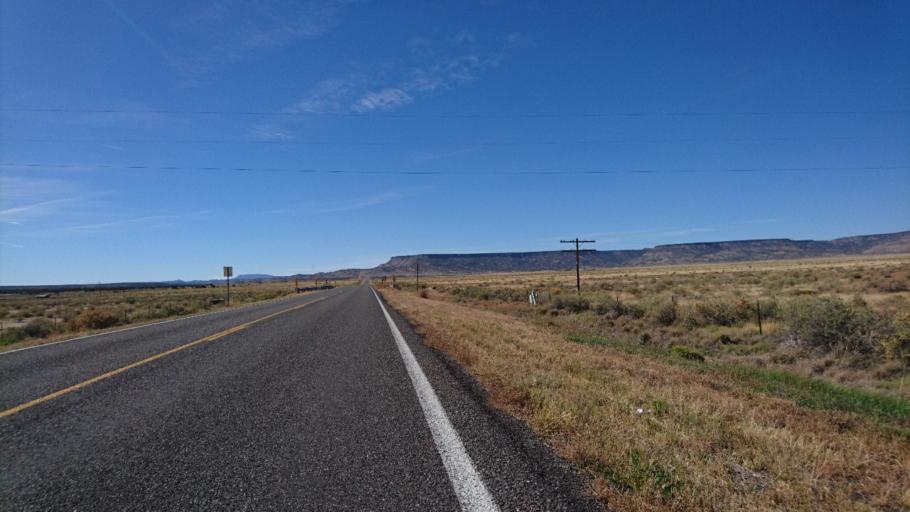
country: US
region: New Mexico
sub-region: Cibola County
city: Skyline-Ganipa
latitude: 35.0825
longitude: -107.6098
